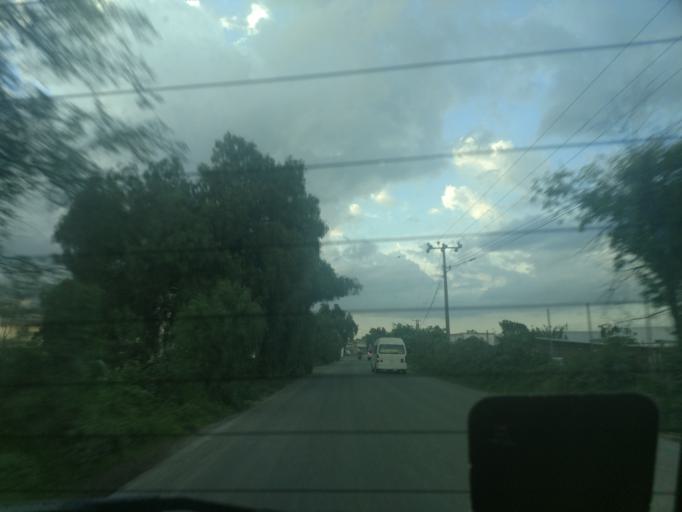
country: MX
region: Mexico
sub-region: Cuautitlan
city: Barrio Tlatenco
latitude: 19.7555
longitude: -99.2012
